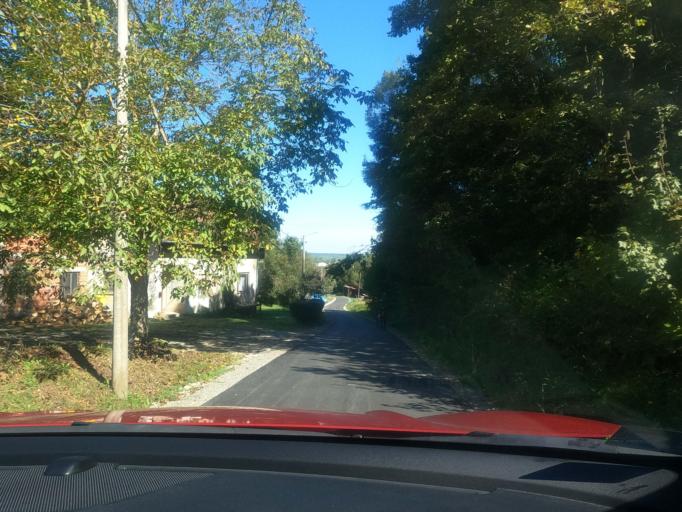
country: HR
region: Sisacko-Moslavacka
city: Petrinja
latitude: 45.4270
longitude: 16.2670
